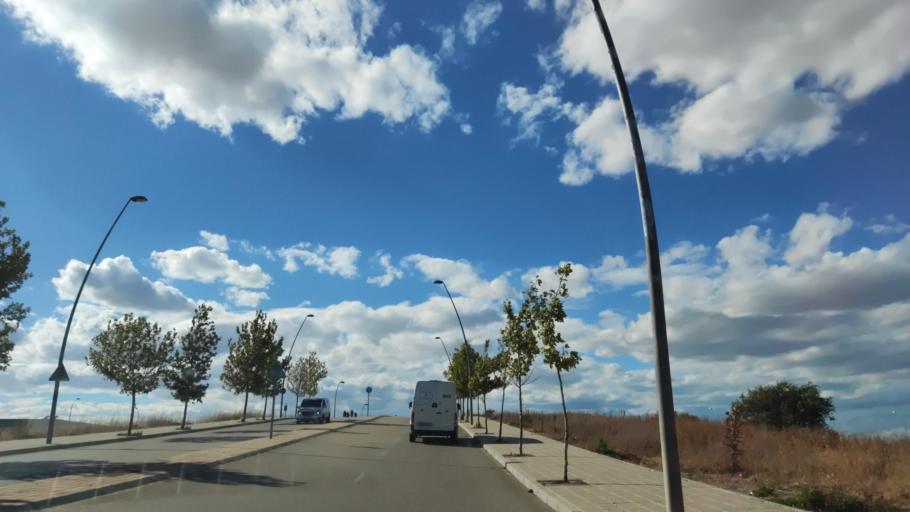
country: ES
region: Madrid
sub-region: Provincia de Madrid
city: Pinto
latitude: 40.2872
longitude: -3.6769
